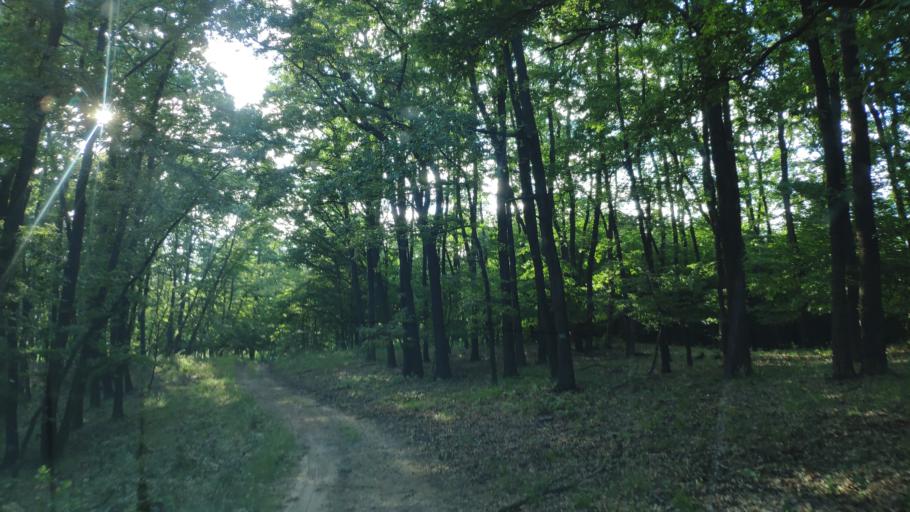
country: HU
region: Borsod-Abauj-Zemplen
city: Arlo
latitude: 48.2445
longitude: 20.1377
